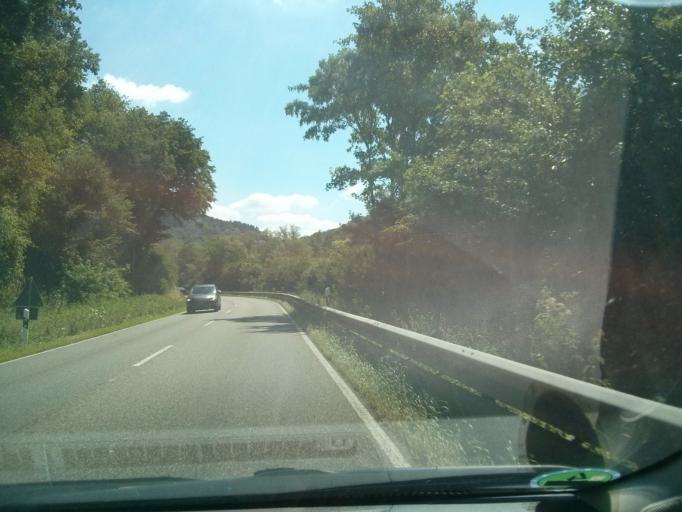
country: DE
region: Rheinland-Pfalz
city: Ahrbruck
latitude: 50.5010
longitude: 6.9803
